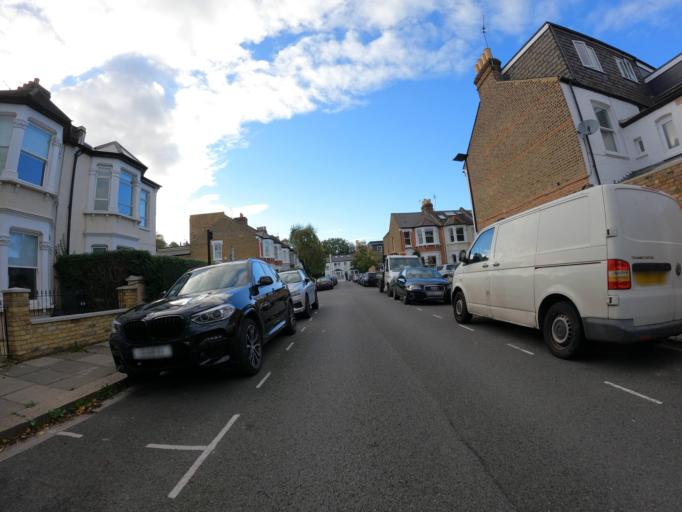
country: GB
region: England
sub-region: Greater London
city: Acton
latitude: 51.4867
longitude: -0.2749
